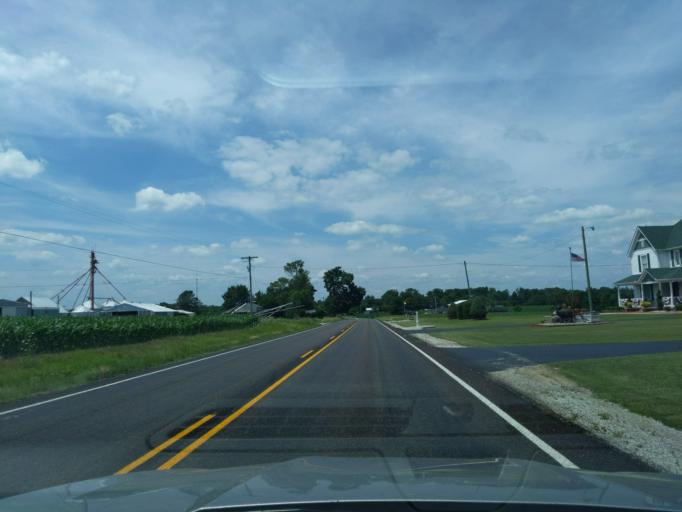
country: US
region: Indiana
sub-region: Decatur County
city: Greensburg
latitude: 39.2614
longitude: -85.3733
